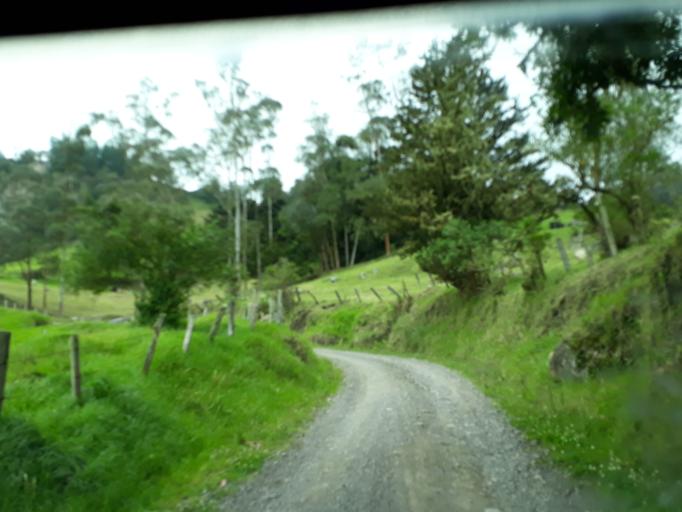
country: CO
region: Cundinamarca
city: Carmen de Carupa
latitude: 5.3757
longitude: -73.9762
